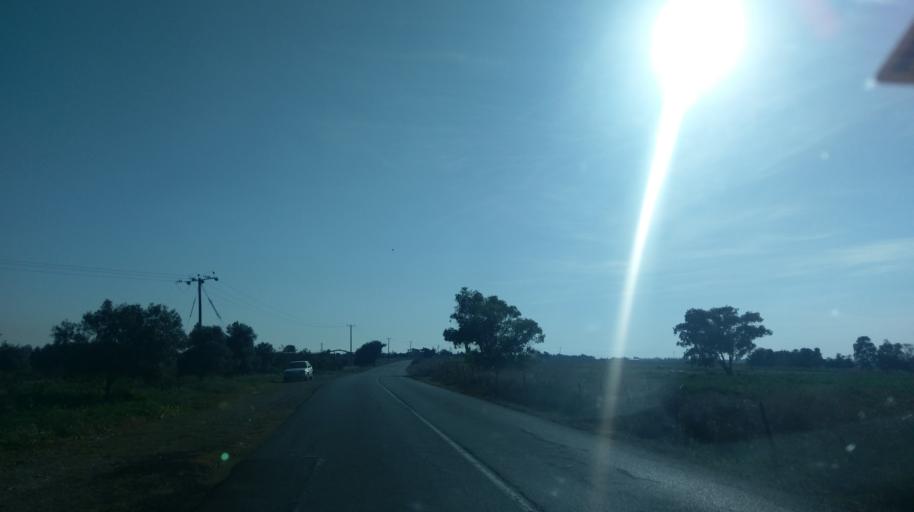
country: CY
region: Larnaka
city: Pergamos
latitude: 35.0656
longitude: 33.7148
